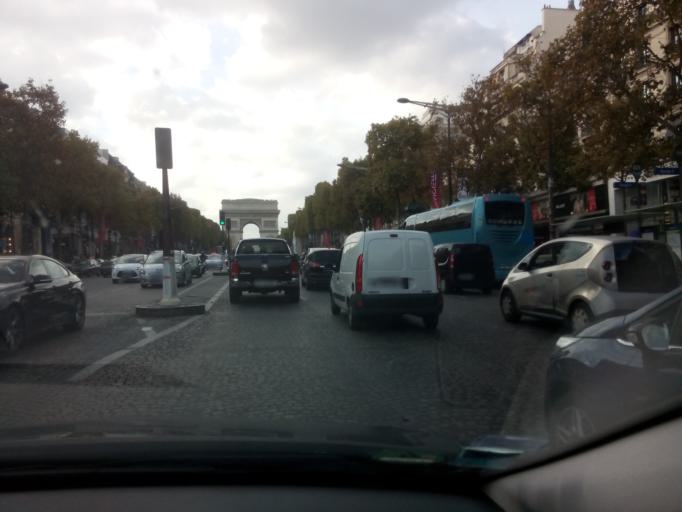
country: FR
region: Ile-de-France
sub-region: Departement des Hauts-de-Seine
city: Levallois-Perret
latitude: 48.8720
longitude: 2.3007
